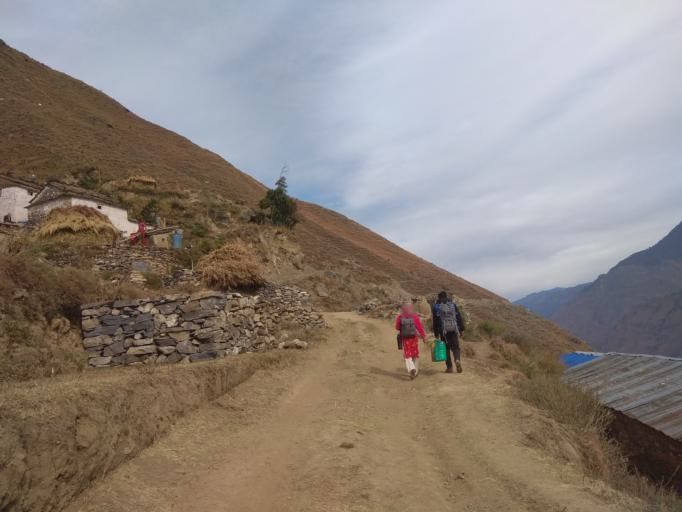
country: NP
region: Mid Western
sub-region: Bheri Zone
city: Dailekh
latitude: 29.2447
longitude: 81.6641
